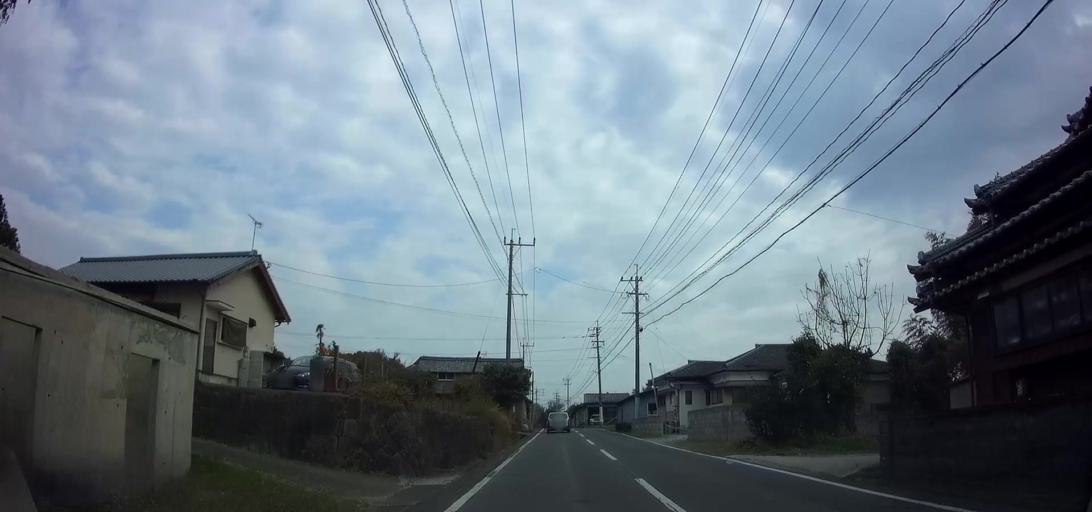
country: JP
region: Nagasaki
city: Shimabara
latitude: 32.6934
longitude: 130.3224
